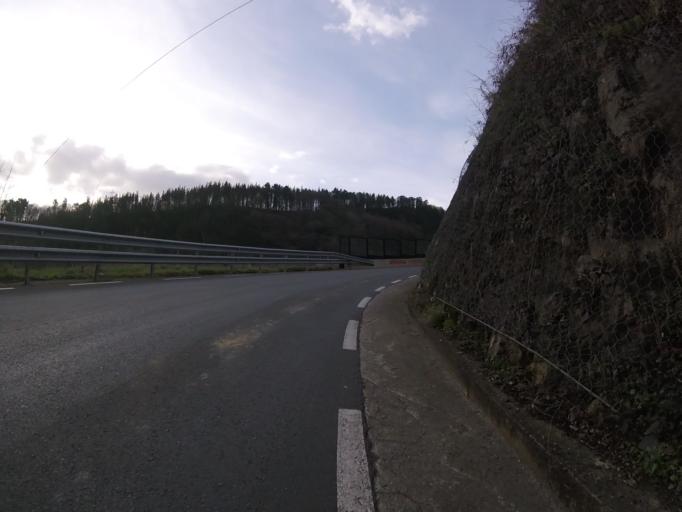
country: ES
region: Basque Country
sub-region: Provincia de Guipuzcoa
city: Anoeta
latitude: 43.1643
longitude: -2.0783
